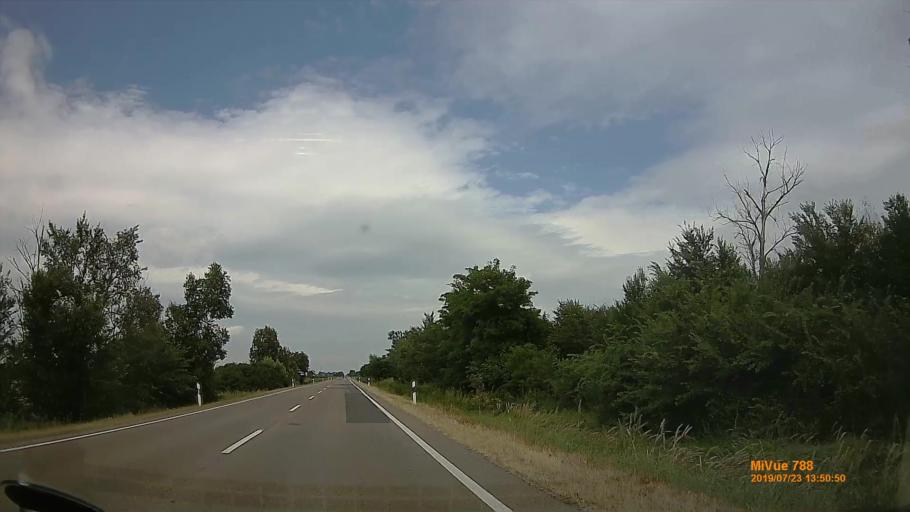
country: HU
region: Hajdu-Bihar
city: Polgar
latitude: 47.8799
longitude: 21.1461
